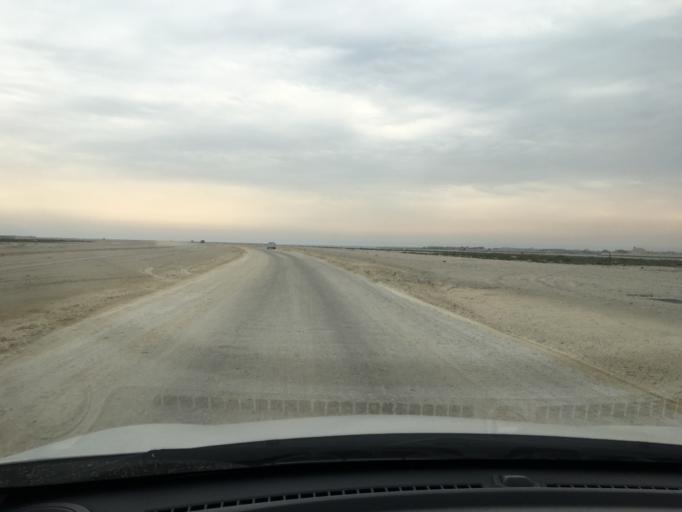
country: BH
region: Central Governorate
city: Dar Kulayb
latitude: 25.8360
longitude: 50.5921
